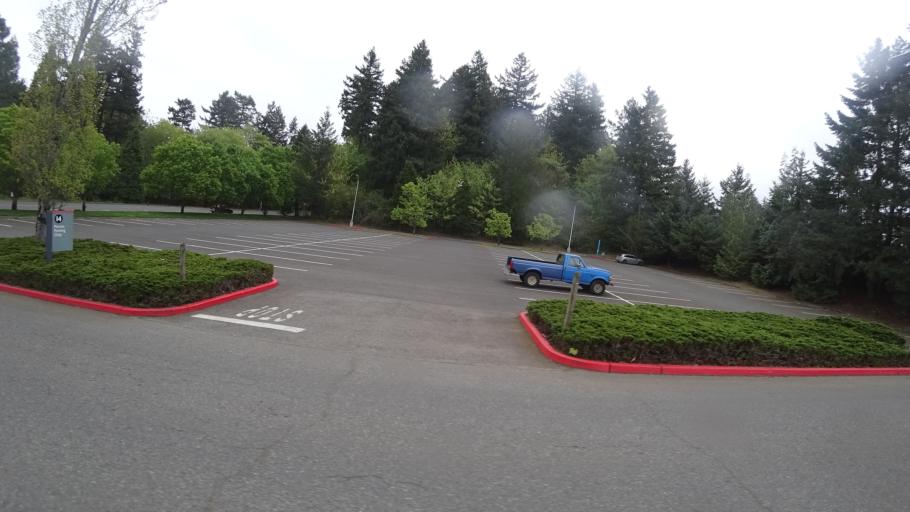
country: US
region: Oregon
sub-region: Washington County
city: Metzger
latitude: 45.4409
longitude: -122.7339
